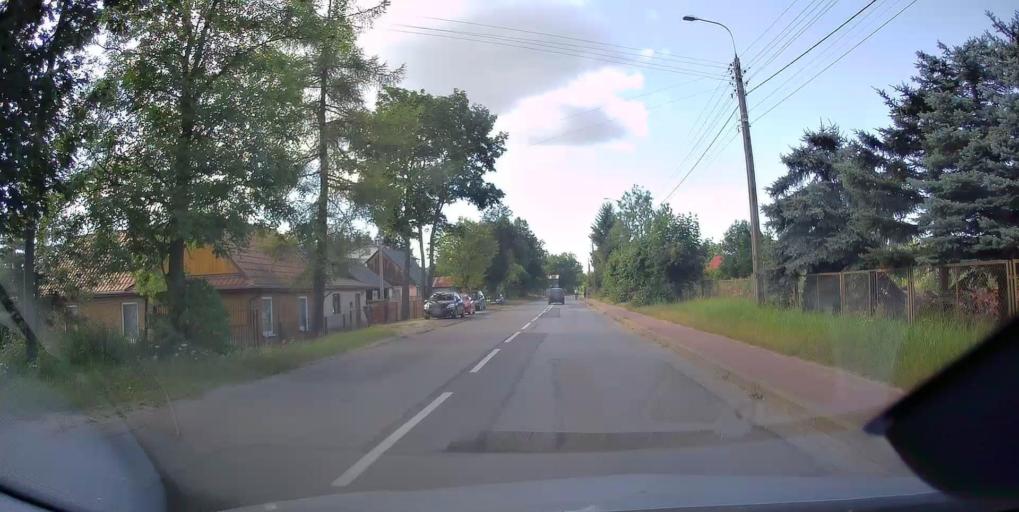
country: PL
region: Swietokrzyskie
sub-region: Powiat skarzyski
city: Suchedniow
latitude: 51.0347
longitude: 20.8378
